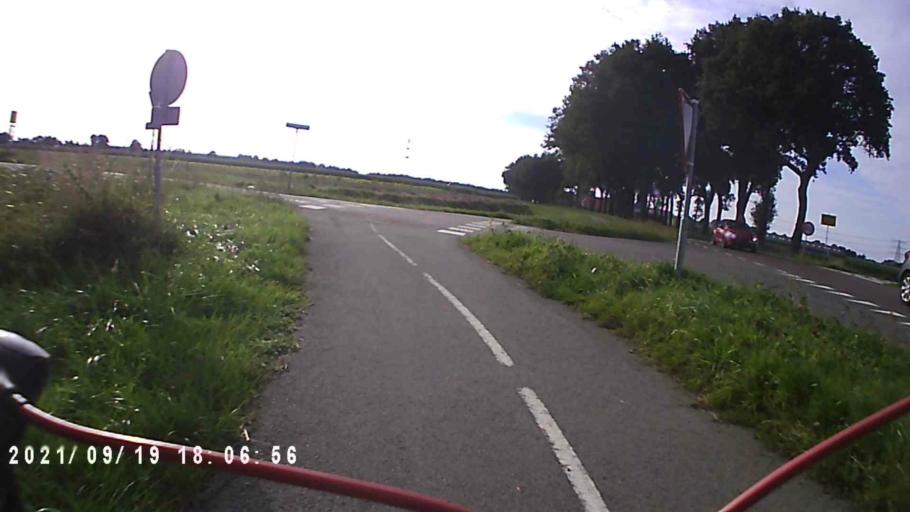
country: NL
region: Groningen
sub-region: Gemeente Delfzijl
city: Delfzijl
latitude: 53.2434
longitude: 6.9094
